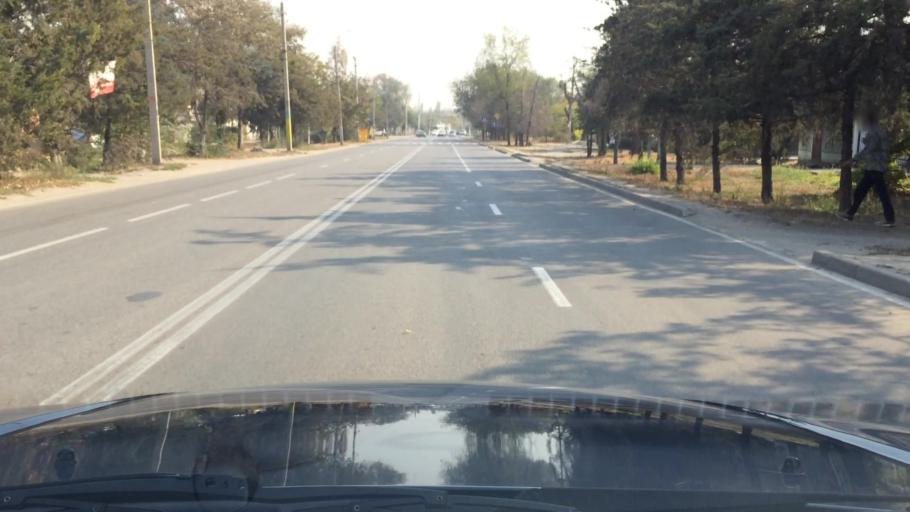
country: KG
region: Chuy
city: Lebedinovka
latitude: 42.8842
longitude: 74.6529
